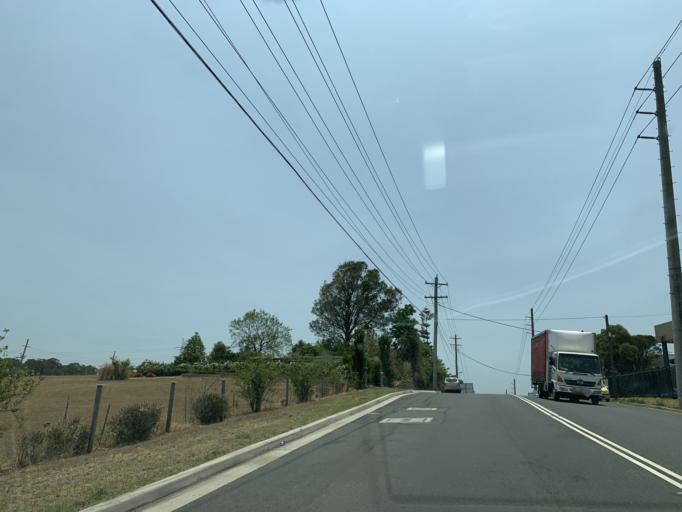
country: AU
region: New South Wales
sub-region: Fairfield
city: Horsley Park
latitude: -33.8403
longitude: 150.8799
